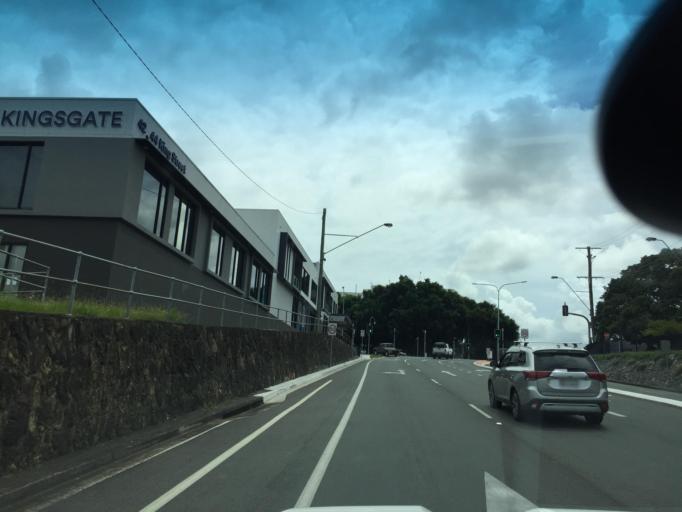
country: AU
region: Queensland
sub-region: Moreton Bay
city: Caboolture
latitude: -27.0859
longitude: 152.9511
